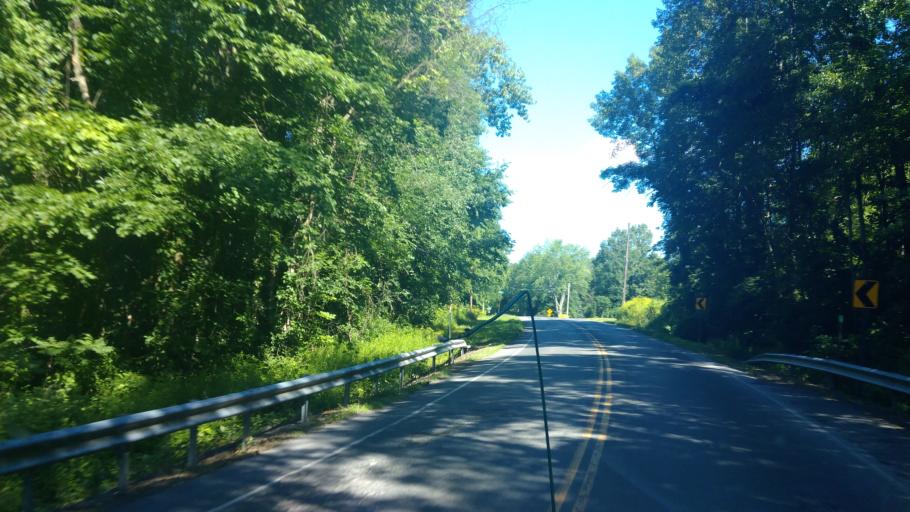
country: US
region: New York
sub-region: Wayne County
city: Lyons
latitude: 43.0227
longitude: -76.9415
